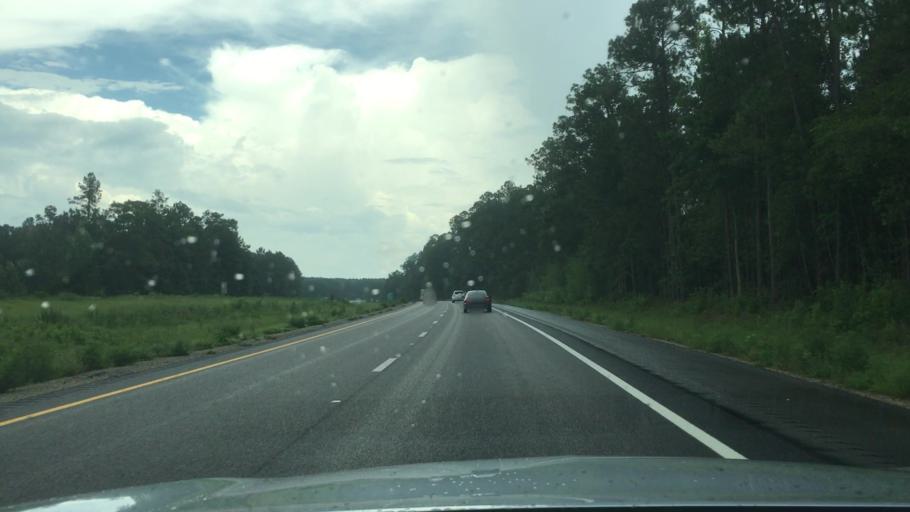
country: US
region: Mississippi
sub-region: Forrest County
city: Hattiesburg
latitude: 31.2290
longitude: -89.3227
